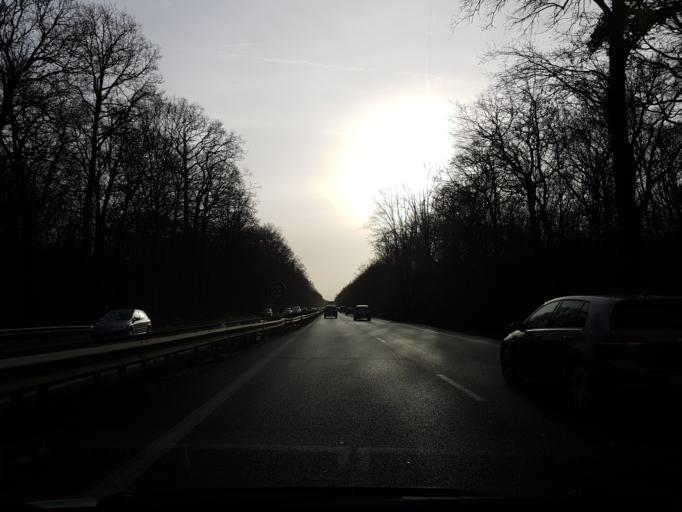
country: FR
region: Ile-de-France
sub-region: Departement de l'Essonne
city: Quincy-sous-Senart
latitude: 48.6565
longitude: 2.5227
